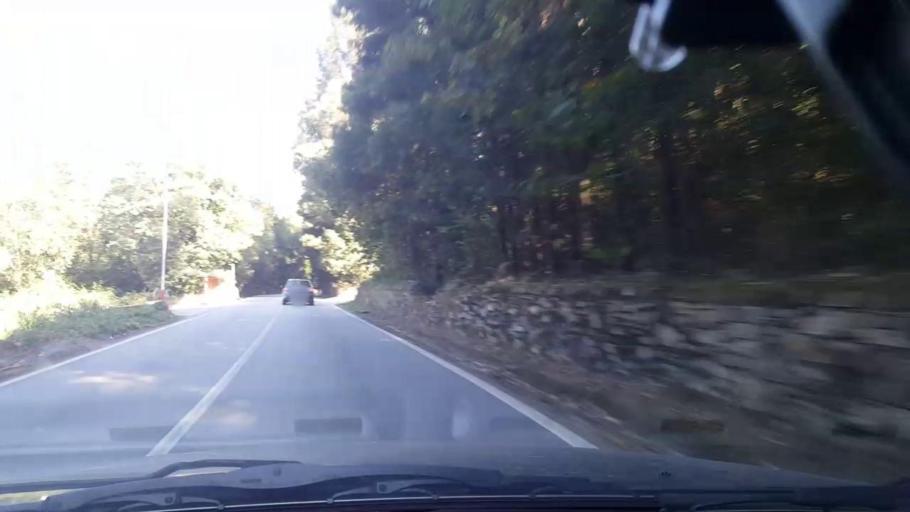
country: PT
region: Porto
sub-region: Maia
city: Gemunde
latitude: 41.3241
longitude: -8.6464
